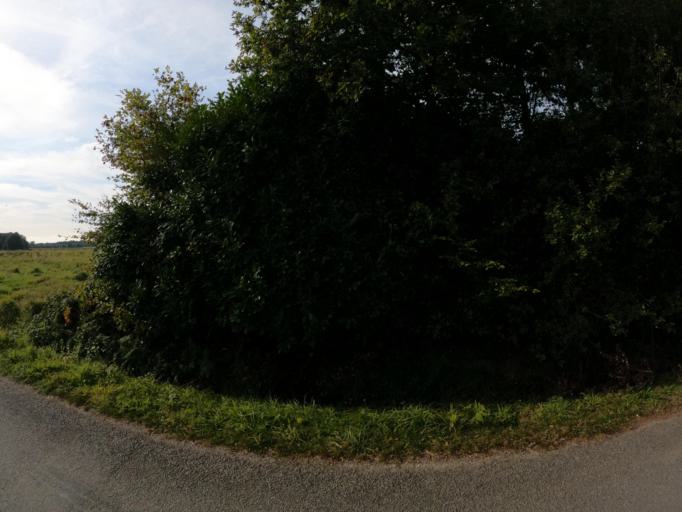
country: FR
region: Brittany
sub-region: Departement du Morbihan
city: Caro
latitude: 47.8870
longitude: -2.3413
